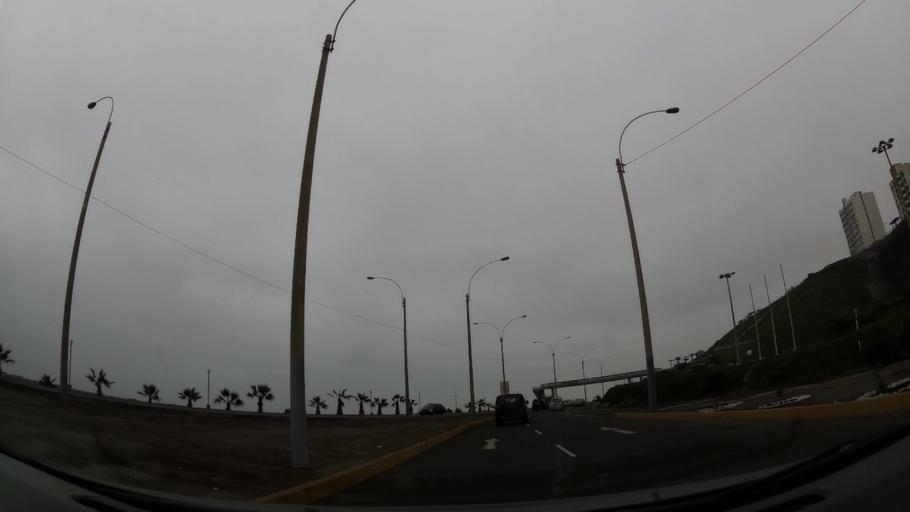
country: PE
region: Lima
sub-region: Lima
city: San Isidro
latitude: -12.0915
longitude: -77.0859
